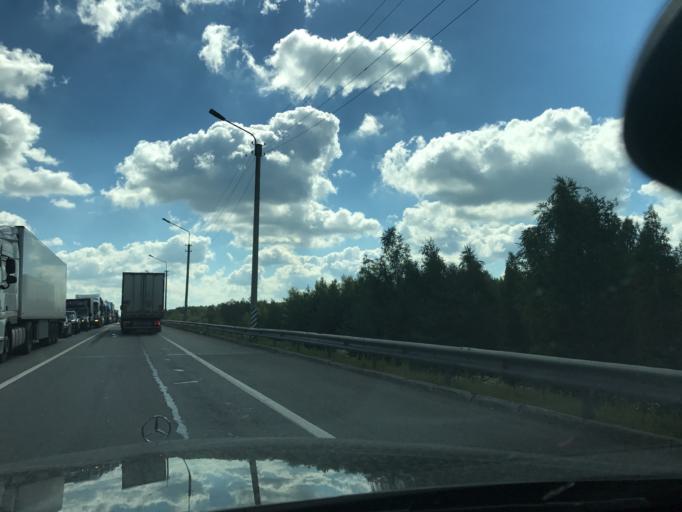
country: RU
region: Vladimir
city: Vorsha
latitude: 56.0767
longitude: 40.2099
